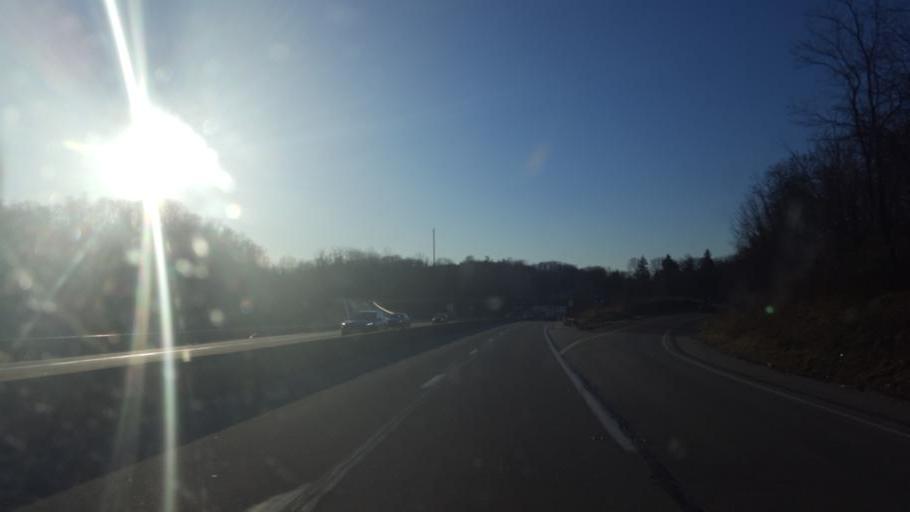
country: US
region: Pennsylvania
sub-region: Washington County
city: Charleroi
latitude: 40.1134
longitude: -79.9385
